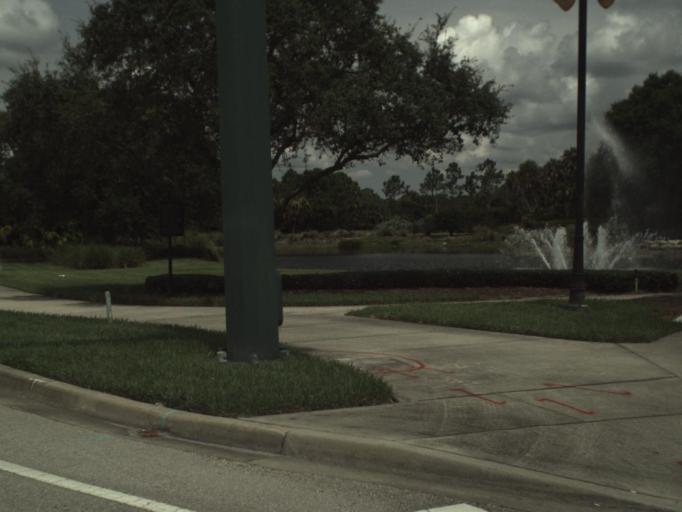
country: US
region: Florida
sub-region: Palm Beach County
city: Palm Beach Gardens
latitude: 26.8393
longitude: -80.1362
